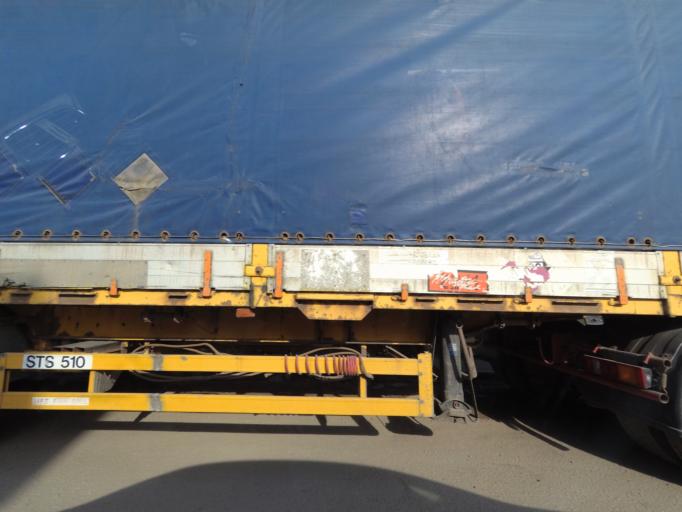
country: RU
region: Moskovskaya
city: Lobnya
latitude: 56.0163
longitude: 37.4363
